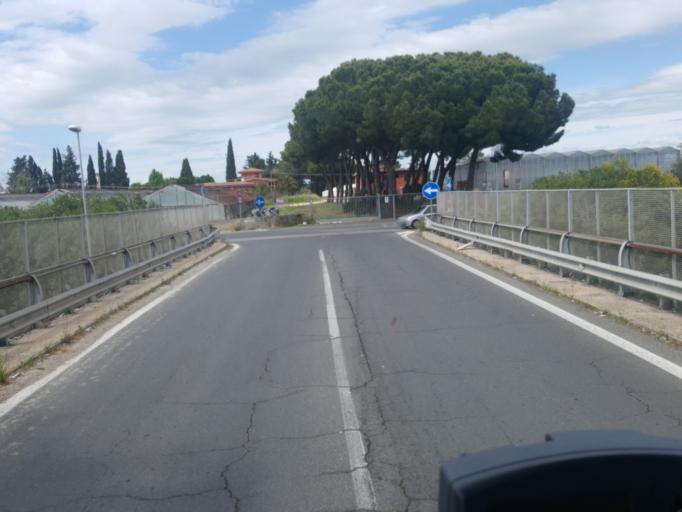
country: IT
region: Latium
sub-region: Citta metropolitana di Roma Capitale
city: La Massimina-Casal Lumbroso
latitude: 41.8818
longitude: 12.3464
